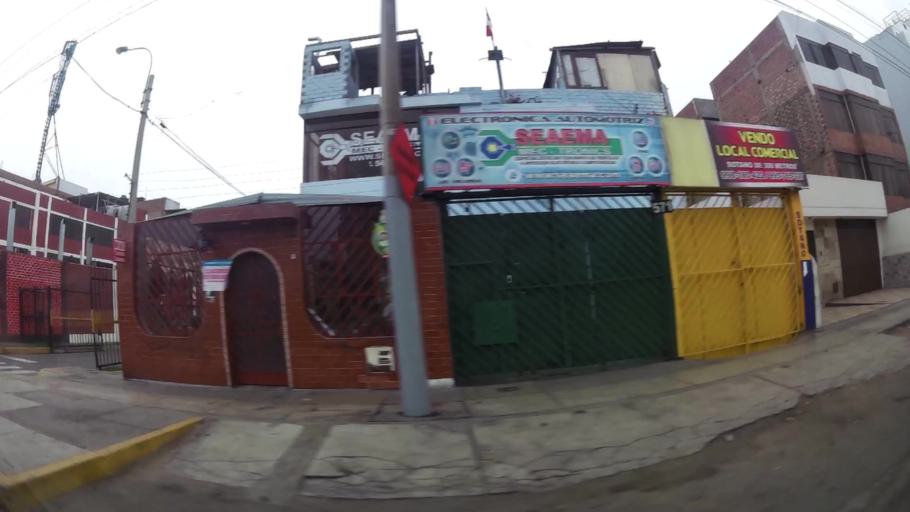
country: PE
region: Callao
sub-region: Callao
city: Callao
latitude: -12.0840
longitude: -77.0828
